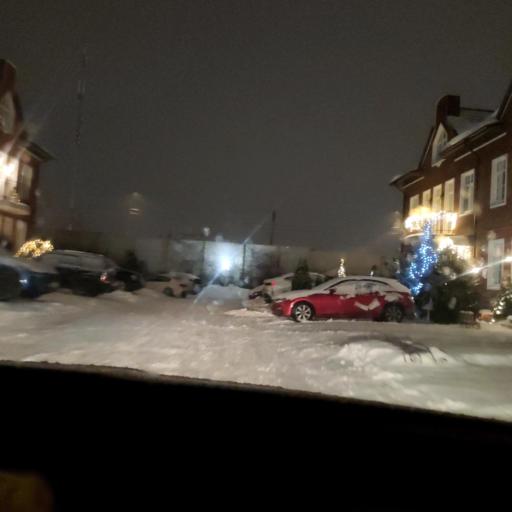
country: RU
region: Moskovskaya
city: Rozhdestveno
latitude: 55.8085
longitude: 36.9776
